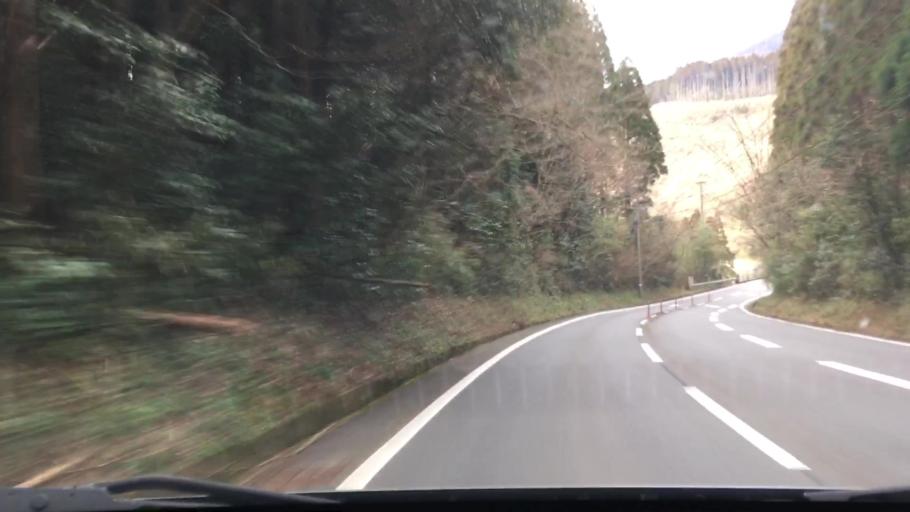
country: JP
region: Miyazaki
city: Nichinan
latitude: 31.7069
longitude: 131.3280
